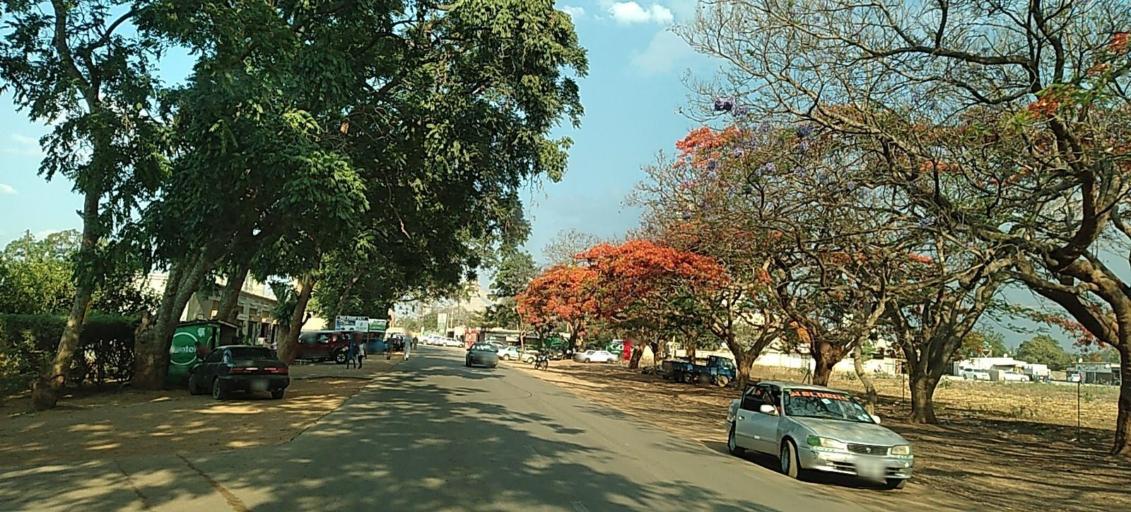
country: ZM
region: Lusaka
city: Lusaka
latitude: -15.5444
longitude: 28.2635
